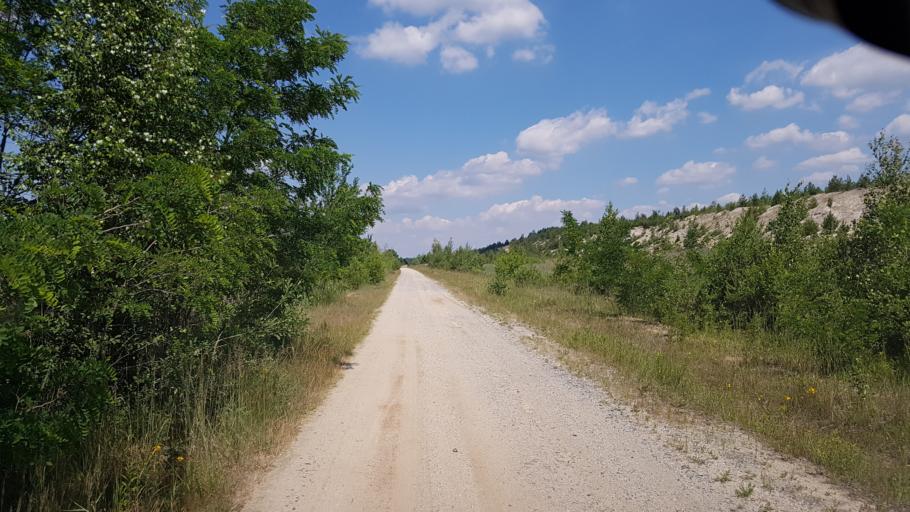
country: DE
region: Brandenburg
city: Sallgast
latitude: 51.5703
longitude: 13.8045
